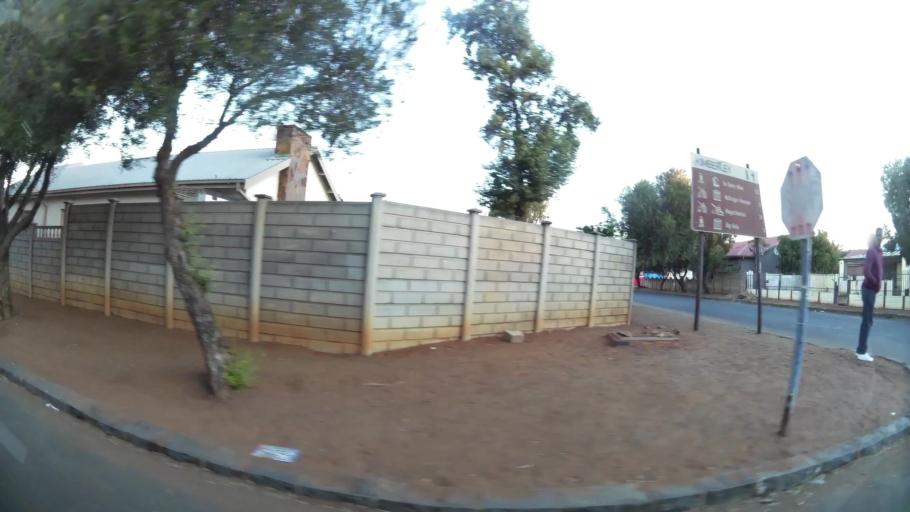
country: ZA
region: Northern Cape
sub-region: Frances Baard District Municipality
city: Kimberley
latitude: -28.7339
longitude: 24.7739
